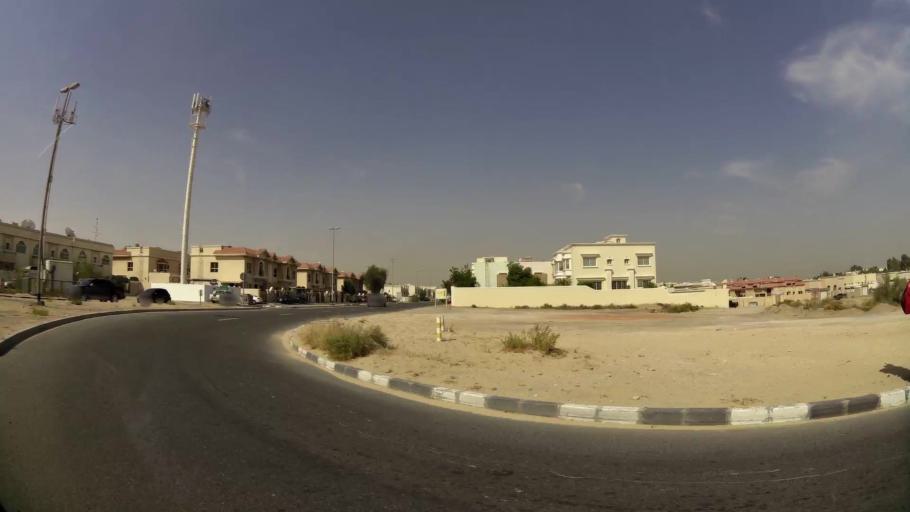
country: AE
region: Ash Shariqah
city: Sharjah
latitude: 25.2195
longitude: 55.4248
